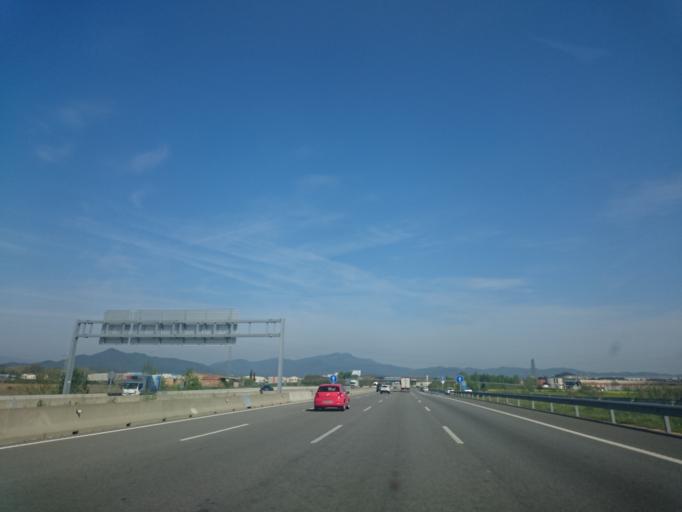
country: ES
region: Catalonia
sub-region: Provincia de Girona
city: Vilablareix
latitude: 41.9605
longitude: 2.7828
